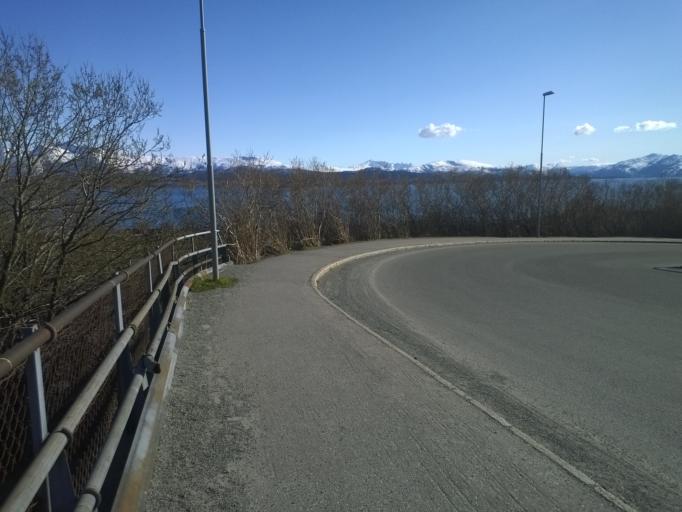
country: NO
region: Nordland
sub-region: Bodo
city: Lopsmarka
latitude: 67.2782
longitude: 14.5101
